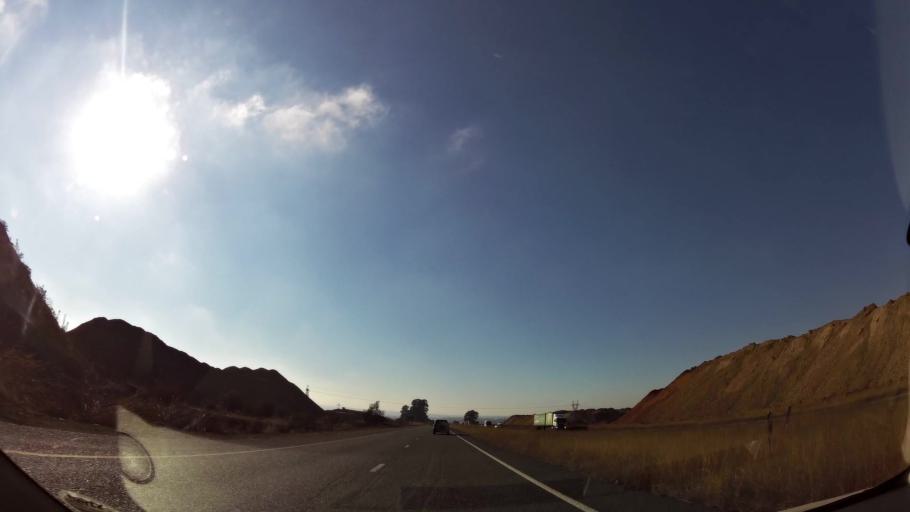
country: ZA
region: Mpumalanga
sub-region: Nkangala District Municipality
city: Witbank
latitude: -26.0179
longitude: 28.9746
